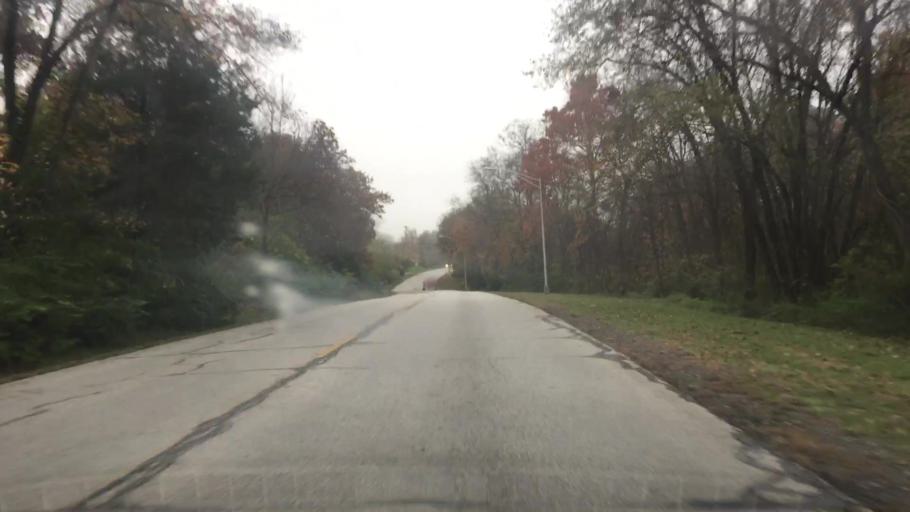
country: US
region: Missouri
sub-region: Callaway County
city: Fulton
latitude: 38.8418
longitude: -91.9546
